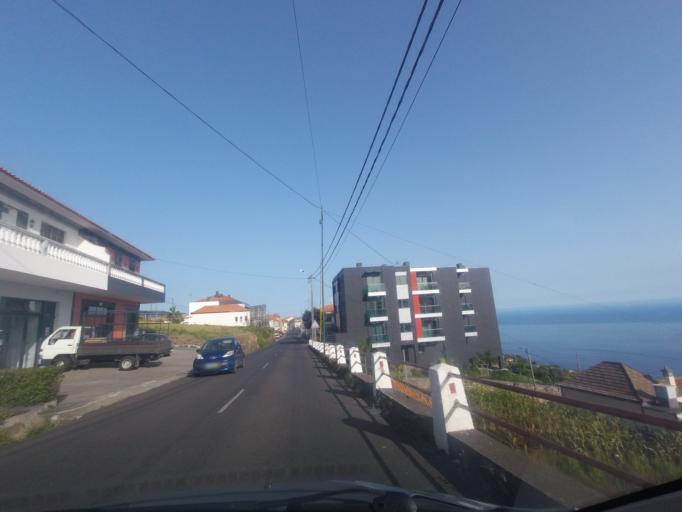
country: PT
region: Madeira
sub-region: Calheta
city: Arco da Calheta
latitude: 32.6984
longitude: -17.1204
